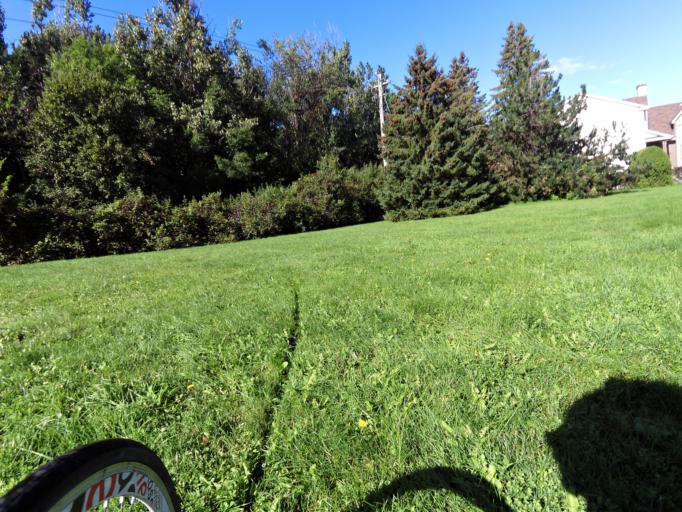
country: CA
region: Ontario
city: Bells Corners
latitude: 45.3132
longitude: -75.8369
